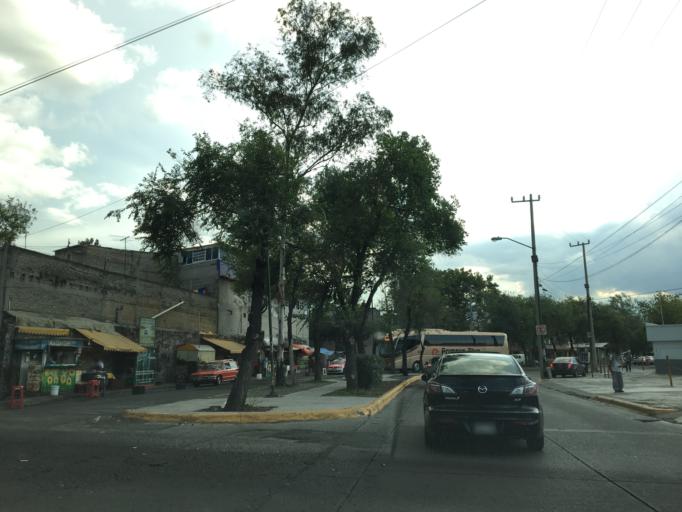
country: MX
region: Mexico
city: Colonia Lindavista
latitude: 19.4778
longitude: -99.1382
